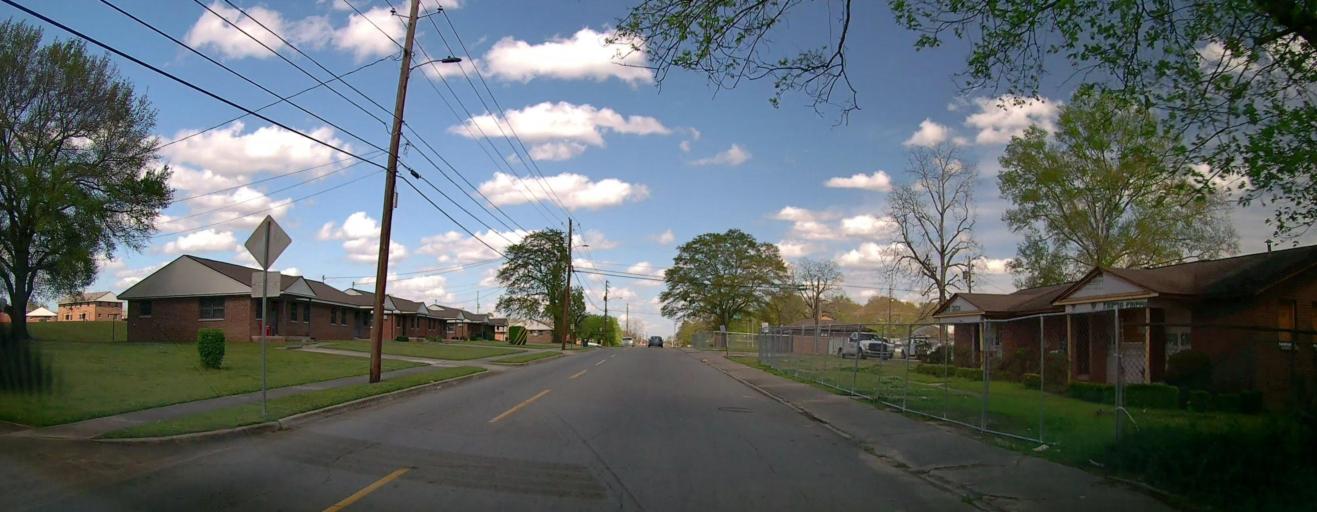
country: US
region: Georgia
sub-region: Bibb County
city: Macon
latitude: 32.8458
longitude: -83.6106
